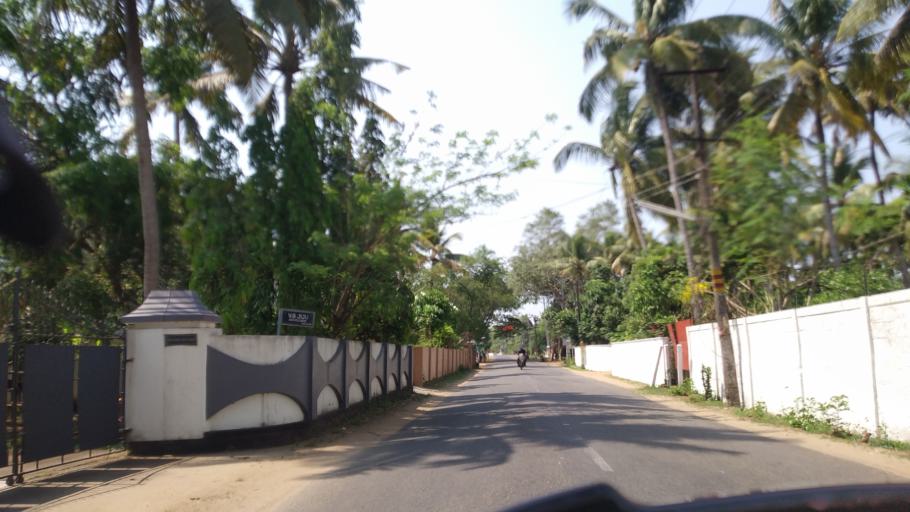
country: IN
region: Kerala
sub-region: Thrissur District
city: Kodungallur
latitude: 10.2612
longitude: 76.1445
